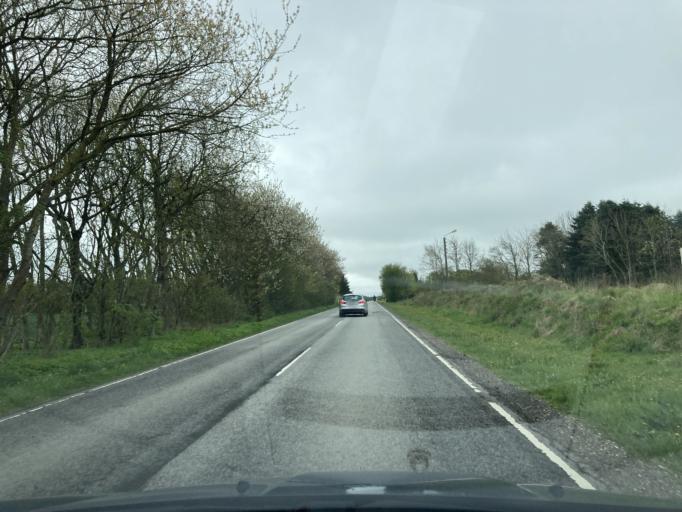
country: DK
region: North Denmark
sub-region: Thisted Kommune
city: Hurup
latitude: 56.8471
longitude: 8.3655
